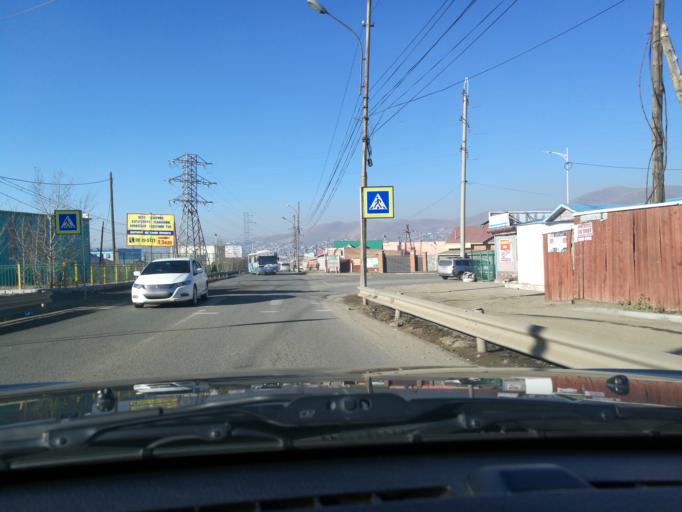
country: MN
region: Ulaanbaatar
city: Ulaanbaatar
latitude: 47.9792
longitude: 106.9349
